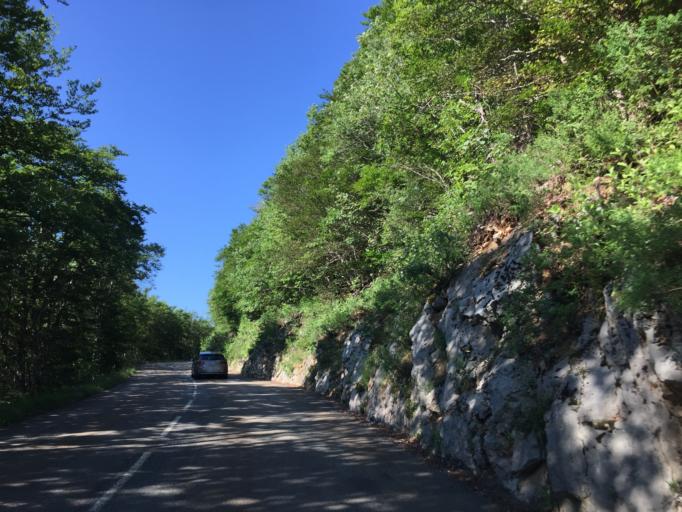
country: FR
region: Rhone-Alpes
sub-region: Departement de la Drome
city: Saint-Laurent-en-Royans
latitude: 44.9170
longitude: 5.3710
